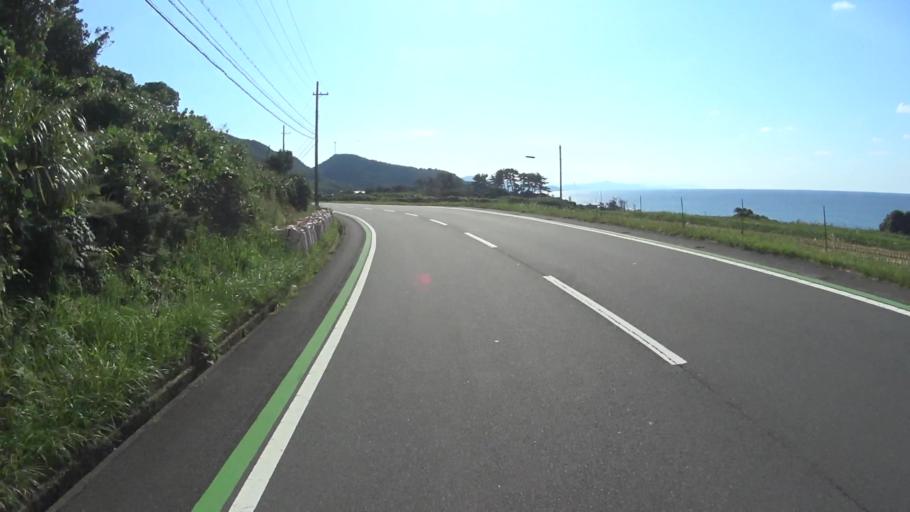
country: JP
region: Kyoto
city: Miyazu
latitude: 35.7241
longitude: 135.0854
